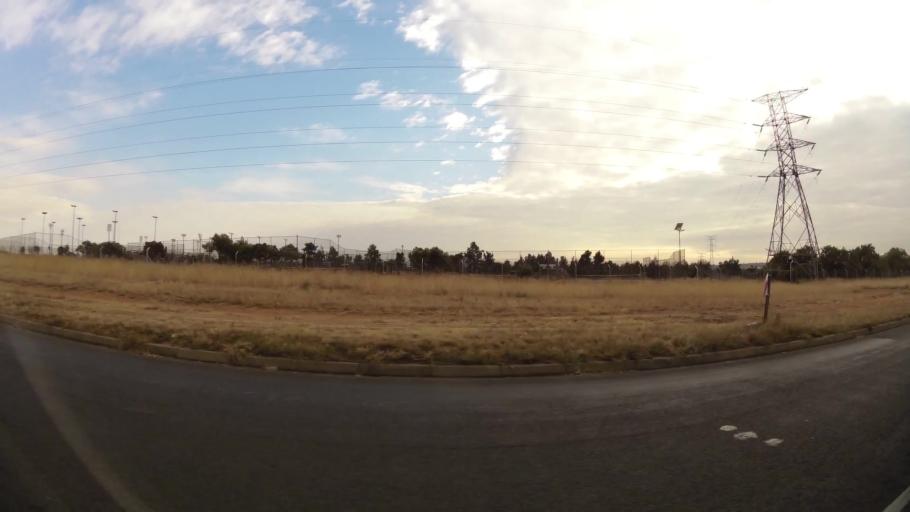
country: ZA
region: Orange Free State
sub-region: Mangaung Metropolitan Municipality
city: Bloemfontein
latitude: -29.1116
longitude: 26.1758
